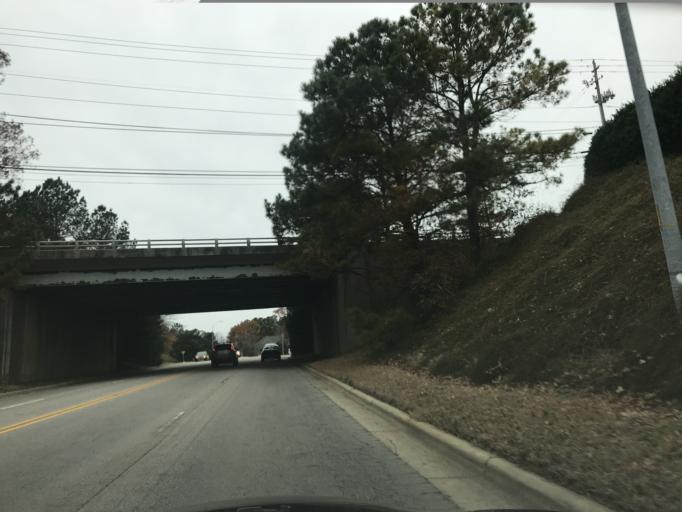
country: US
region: North Carolina
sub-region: Wake County
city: West Raleigh
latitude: 35.7997
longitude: -78.6596
